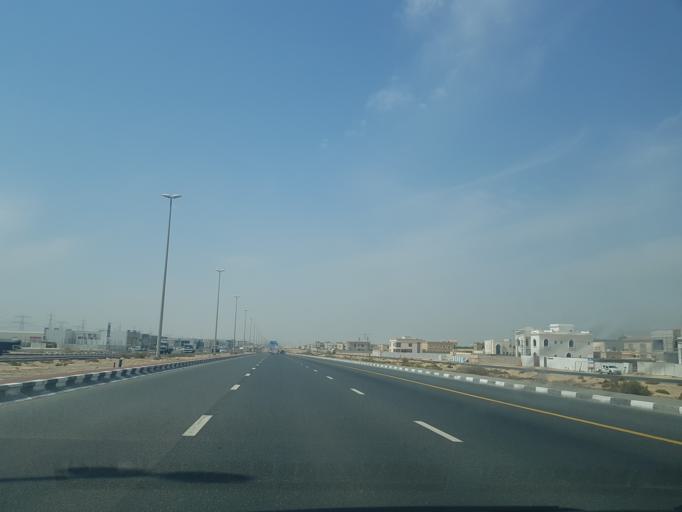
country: AE
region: Ash Shariqah
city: Sharjah
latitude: 25.2632
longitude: 55.5022
